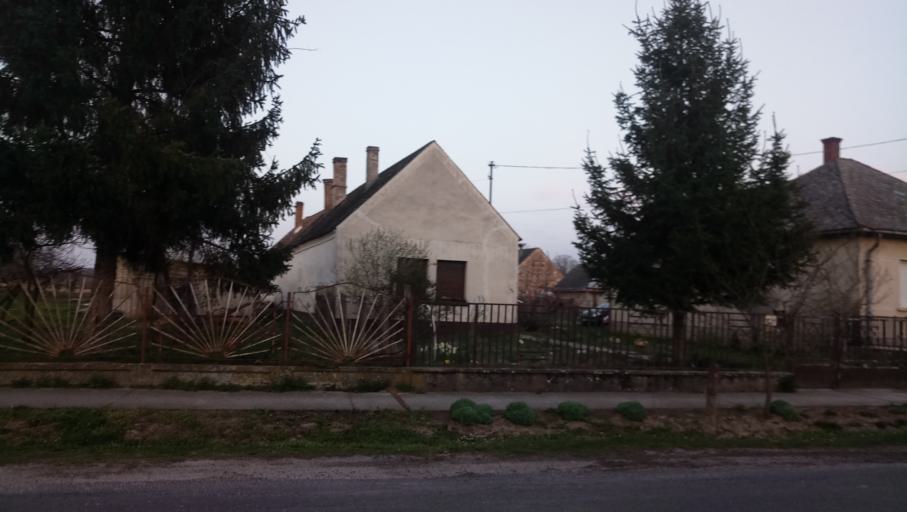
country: HU
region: Somogy
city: Nagybajom
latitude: 46.4165
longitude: 17.5962
